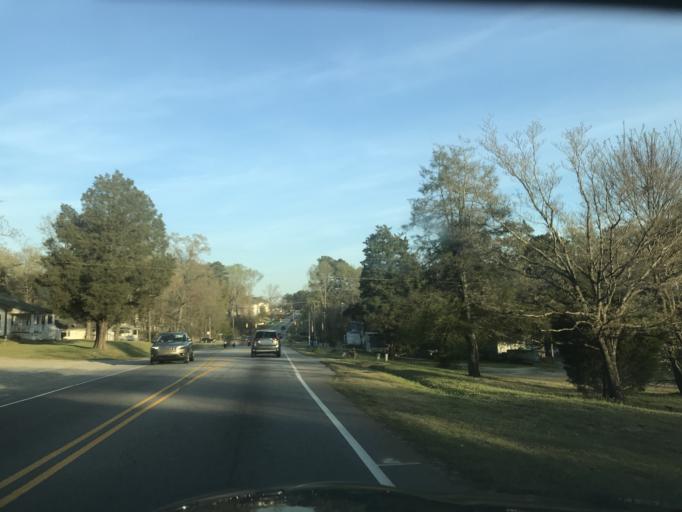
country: US
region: North Carolina
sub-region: Wake County
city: Garner
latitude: 35.7310
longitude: -78.5579
